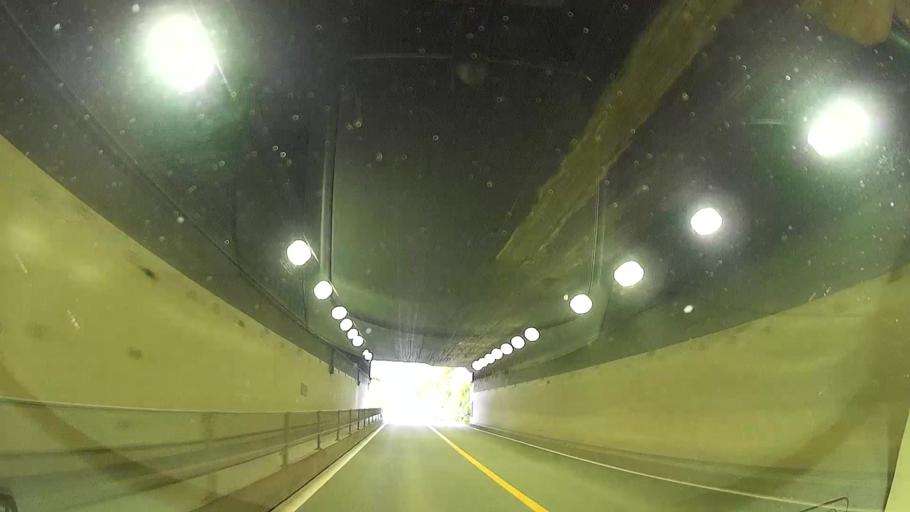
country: JP
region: Kumamoto
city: Ozu
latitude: 32.8381
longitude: 130.8534
